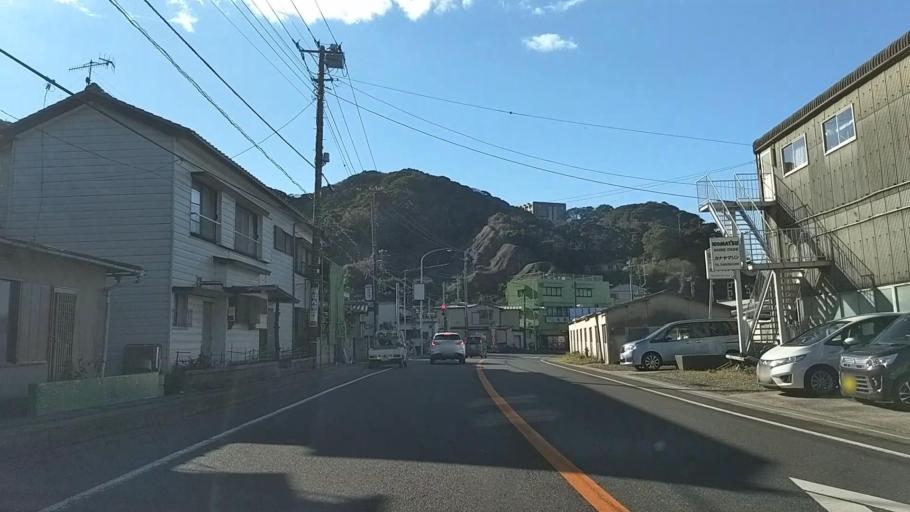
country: JP
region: Chiba
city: Futtsu
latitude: 35.1640
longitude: 139.8227
